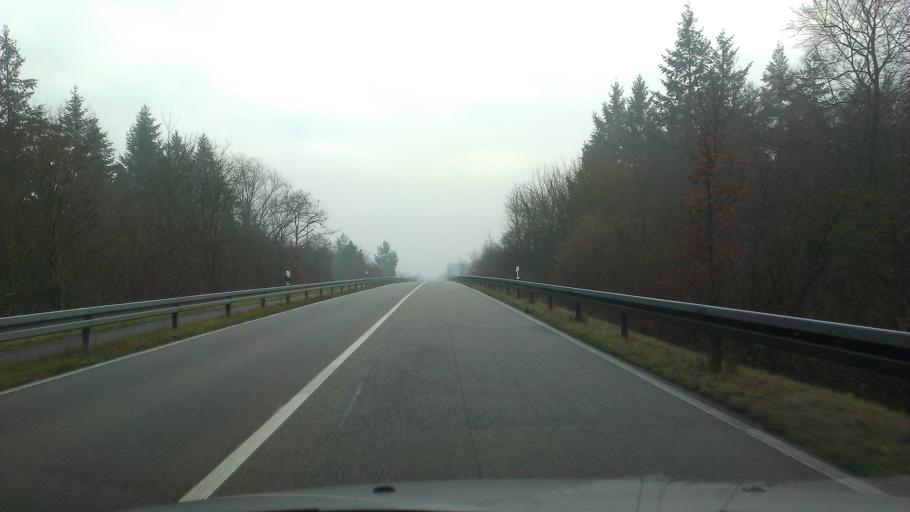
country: DE
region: Baden-Wuerttemberg
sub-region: Karlsruhe Region
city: Hambrucken
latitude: 49.1872
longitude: 8.5188
